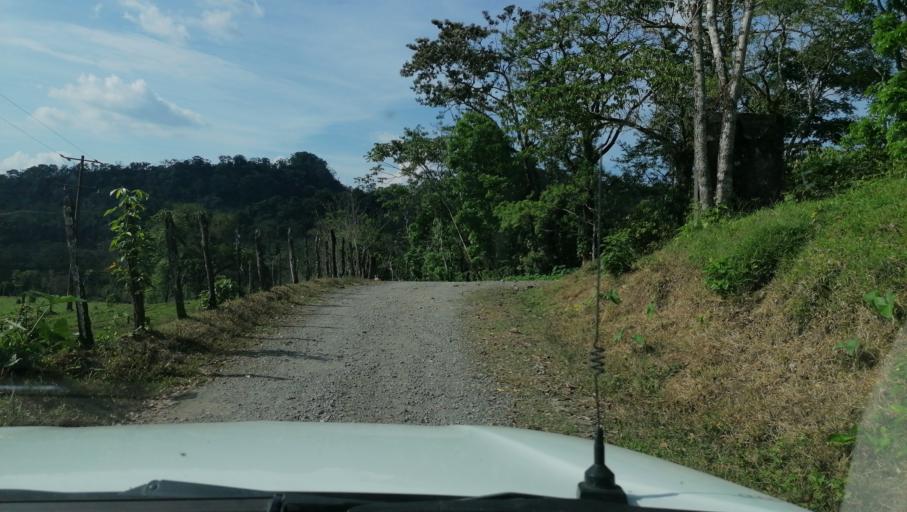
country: MX
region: Chiapas
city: Ostuacan
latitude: 17.4708
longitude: -93.2361
